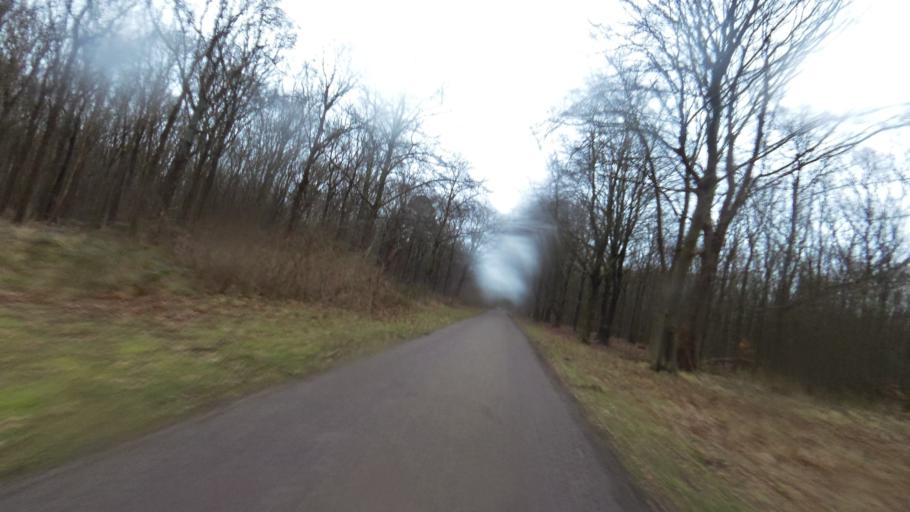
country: NL
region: North Holland
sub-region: Gemeente Bergen
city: Egmond aan Zee
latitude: 52.5762
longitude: 4.6274
